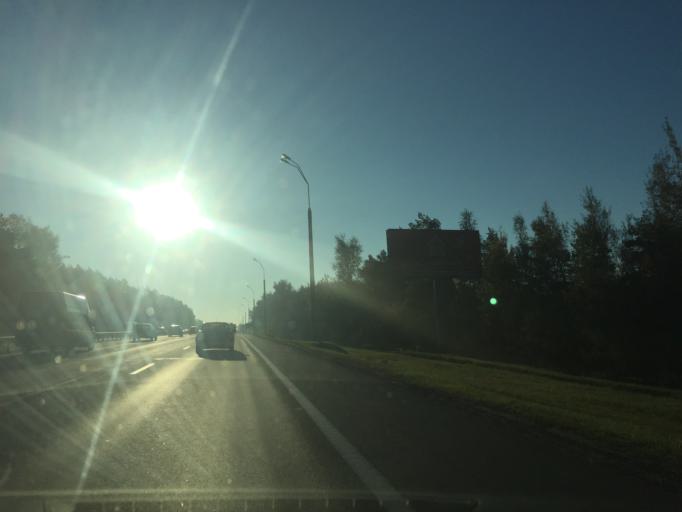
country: BY
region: Minsk
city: Vyaliki Trastsyanets
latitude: 53.8298
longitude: 27.7430
